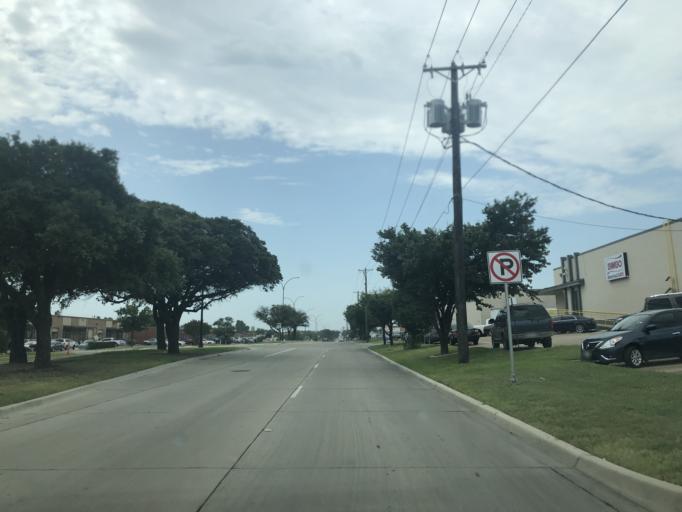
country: US
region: Texas
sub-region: Dallas County
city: Grand Prairie
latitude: 32.7542
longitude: -97.0459
